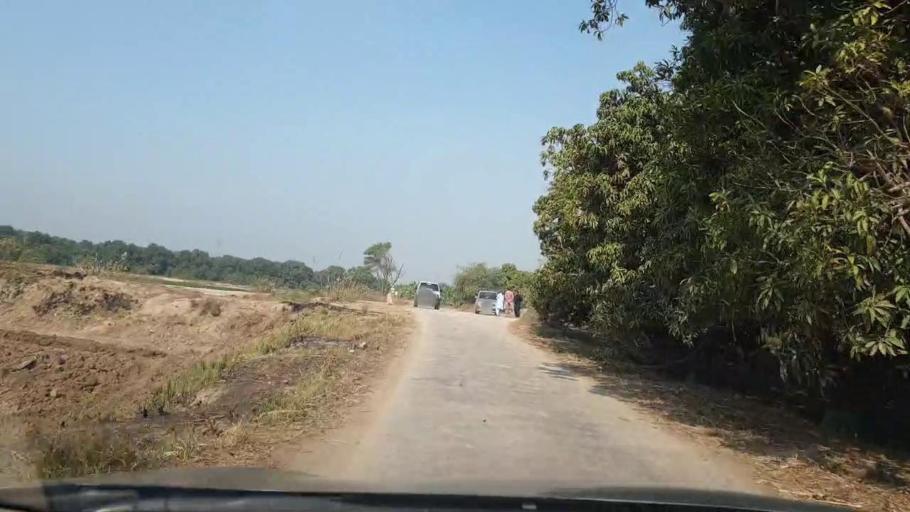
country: PK
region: Sindh
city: Tando Allahyar
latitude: 25.4823
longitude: 68.7918
